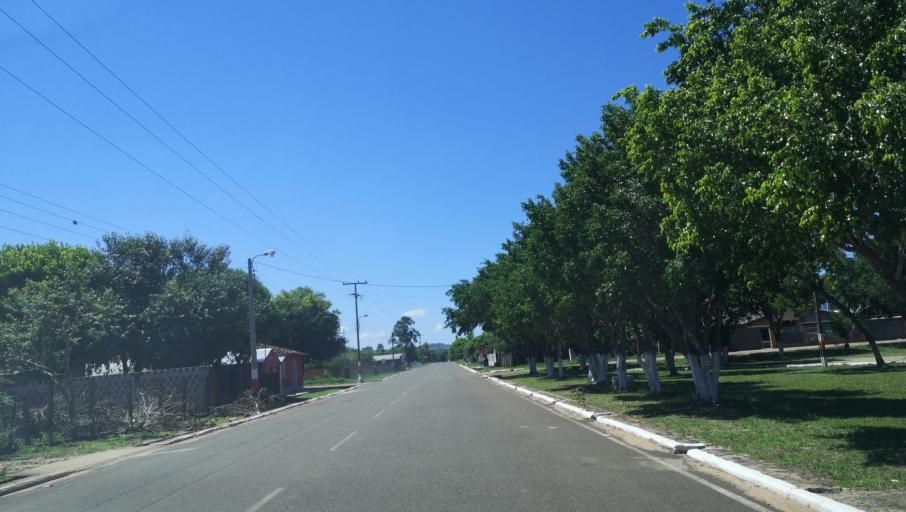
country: PY
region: Caaguazu
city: Carayao
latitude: -25.1973
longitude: -56.3994
